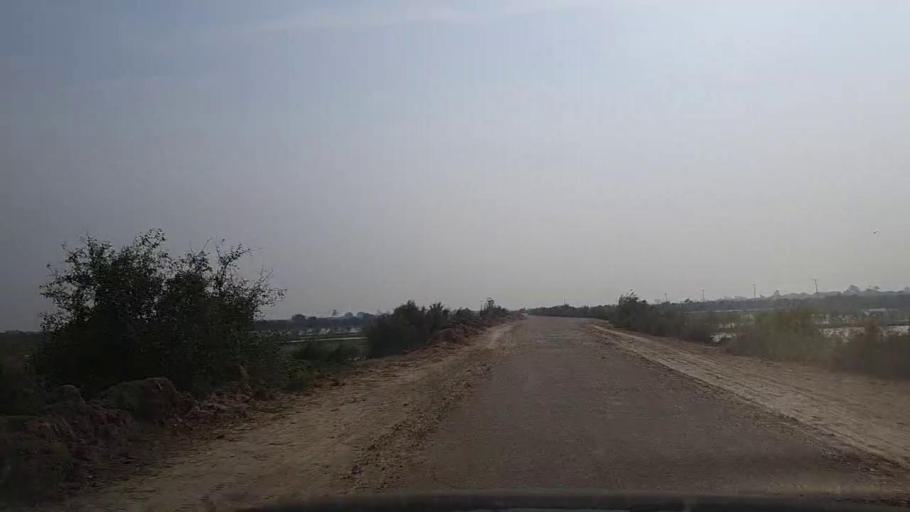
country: PK
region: Sindh
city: Mirpur Sakro
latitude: 24.4007
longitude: 67.7512
